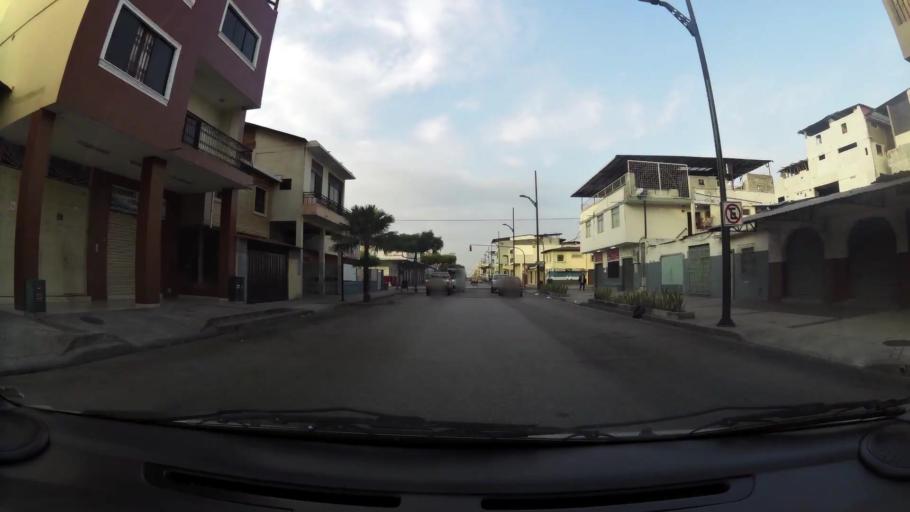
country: EC
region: Guayas
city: Guayaquil
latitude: -2.1970
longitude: -79.8968
